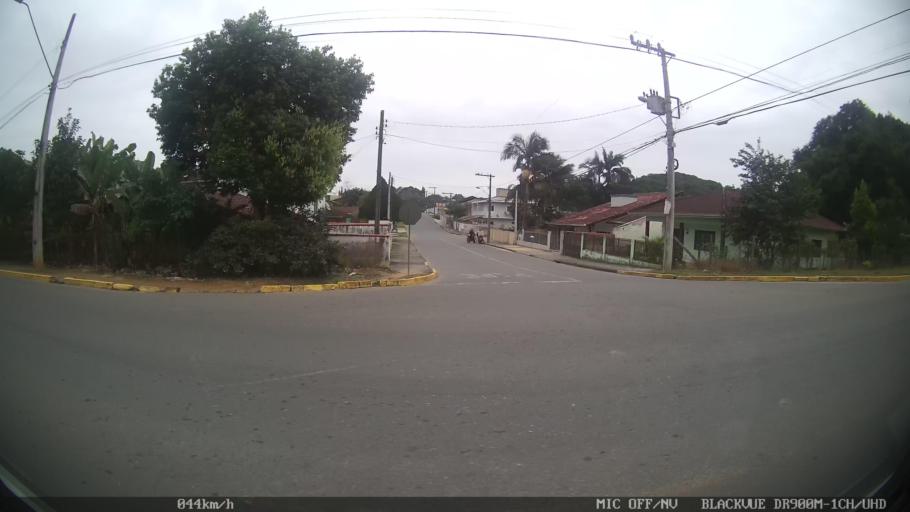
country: BR
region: Santa Catarina
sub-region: Joinville
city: Joinville
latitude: -26.3537
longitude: -48.8387
